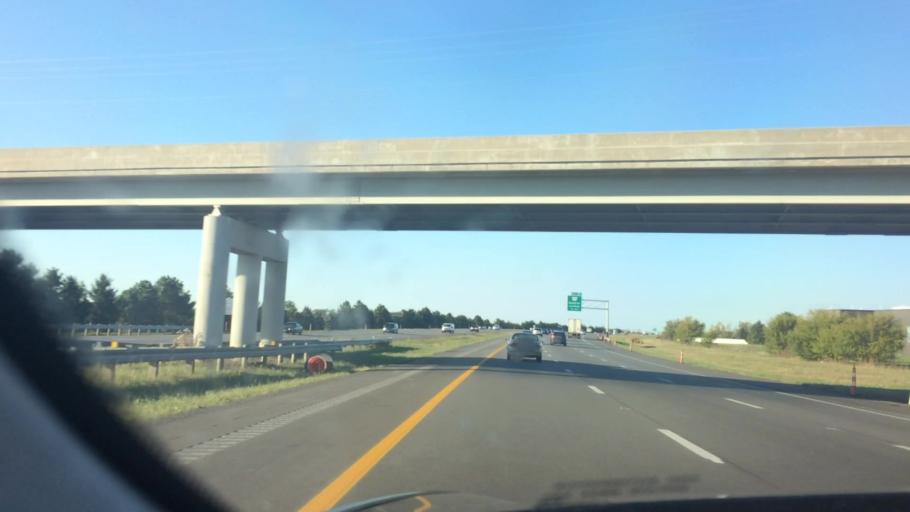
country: US
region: Ohio
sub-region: Wood County
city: Bowling Green
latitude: 41.4432
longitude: -83.6216
